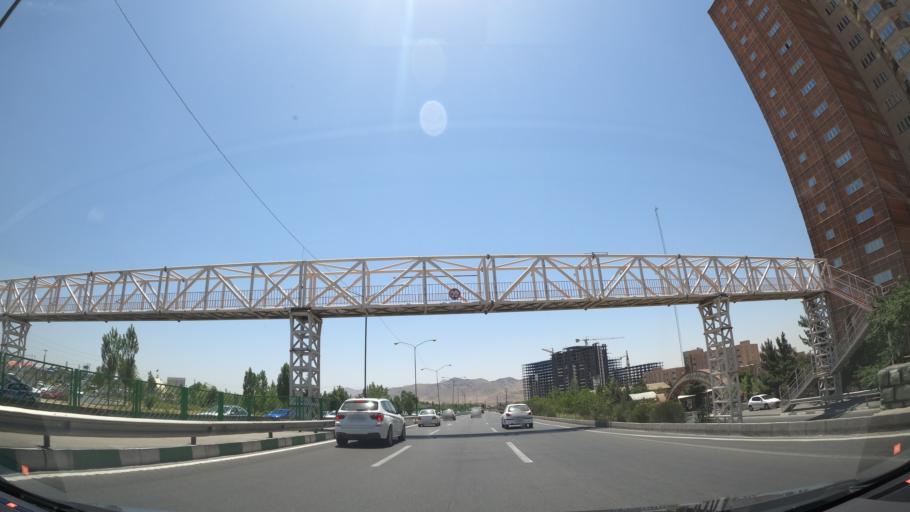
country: IR
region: Tehran
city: Tajrish
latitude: 35.7561
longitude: 51.5759
